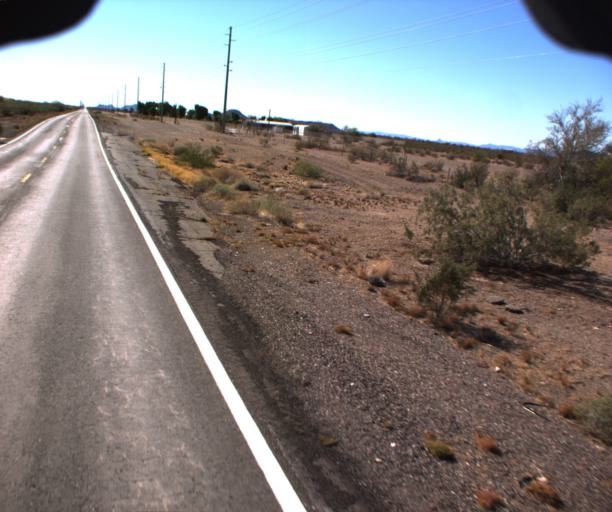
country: US
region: Arizona
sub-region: La Paz County
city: Salome
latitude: 33.8085
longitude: -113.8453
